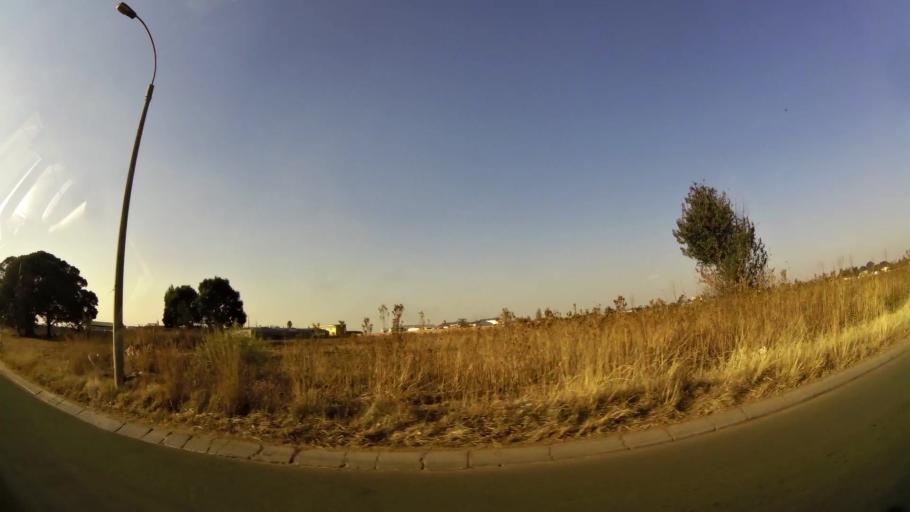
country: ZA
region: Gauteng
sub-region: West Rand District Municipality
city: Randfontein
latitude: -26.2040
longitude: 27.6889
